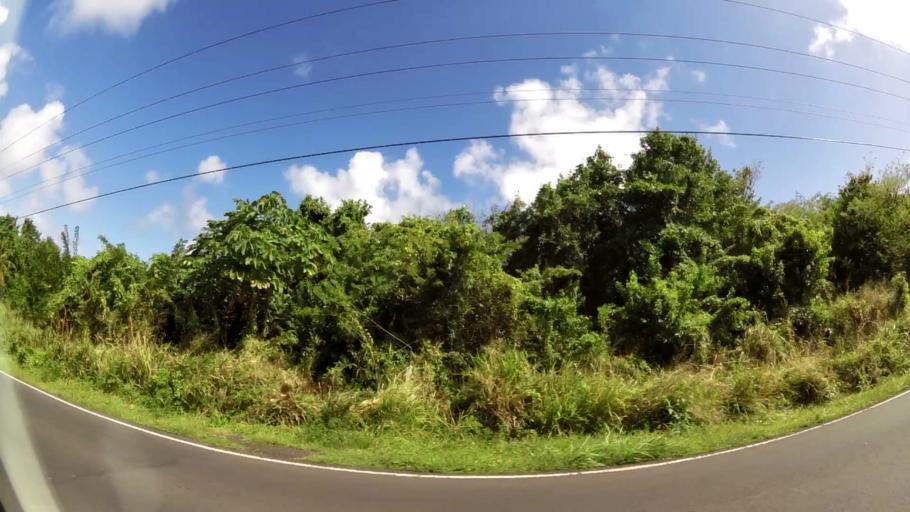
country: LC
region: Micoud Quarter
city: Micoud
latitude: 13.8115
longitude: -60.9022
